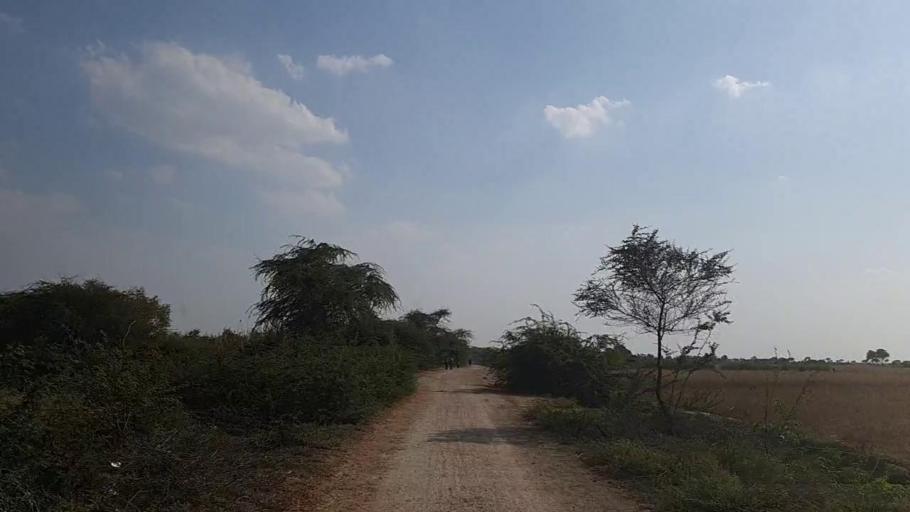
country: PK
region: Sindh
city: Jati
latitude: 24.4786
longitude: 68.3388
